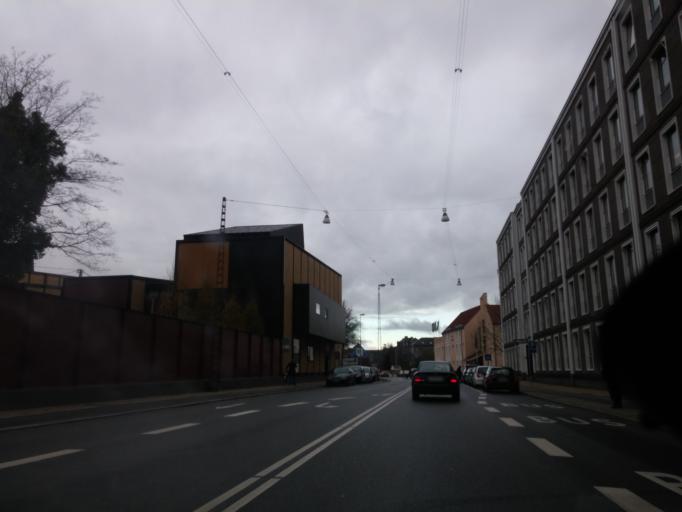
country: DK
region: South Denmark
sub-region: Odense Kommune
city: Odense
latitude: 55.3984
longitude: 10.3943
